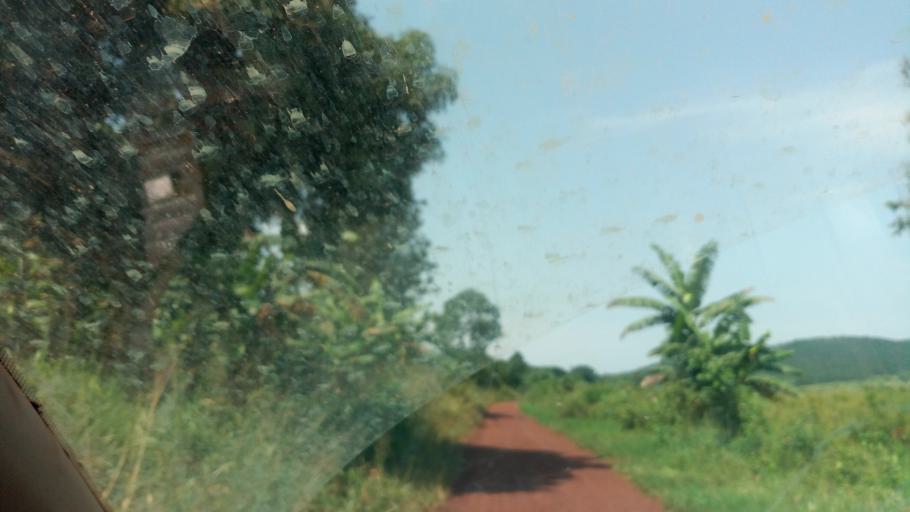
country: UG
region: Western Region
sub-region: Masindi District
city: Masindi
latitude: 1.6562
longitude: 31.8093
